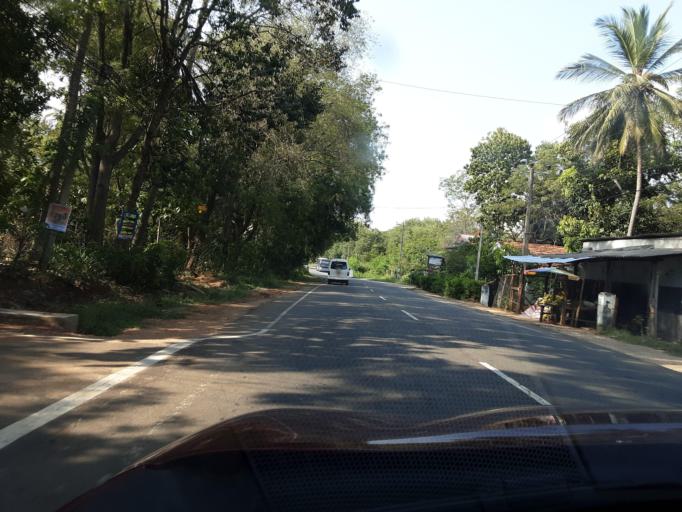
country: LK
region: Uva
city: Haputale
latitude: 6.5869
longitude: 81.1412
